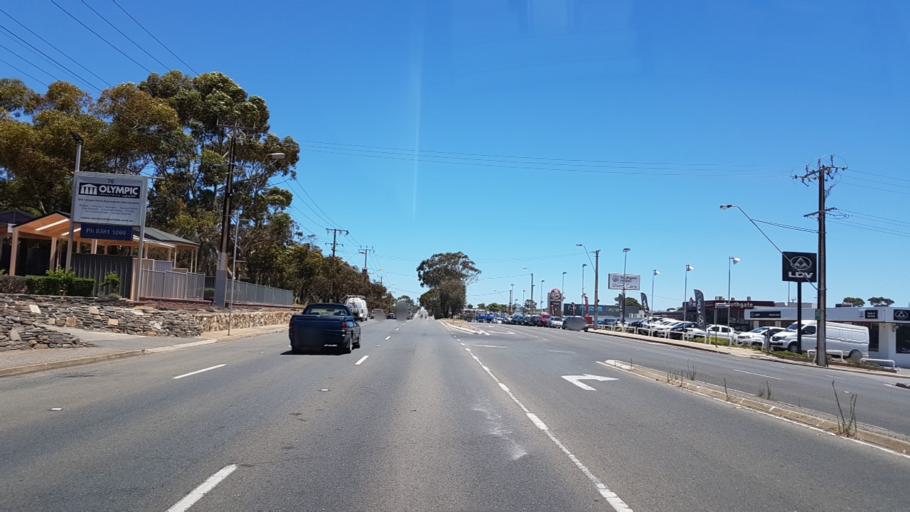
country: AU
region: South Australia
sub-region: Onkaparinga
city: Reynella
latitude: -35.1011
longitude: 138.5311
